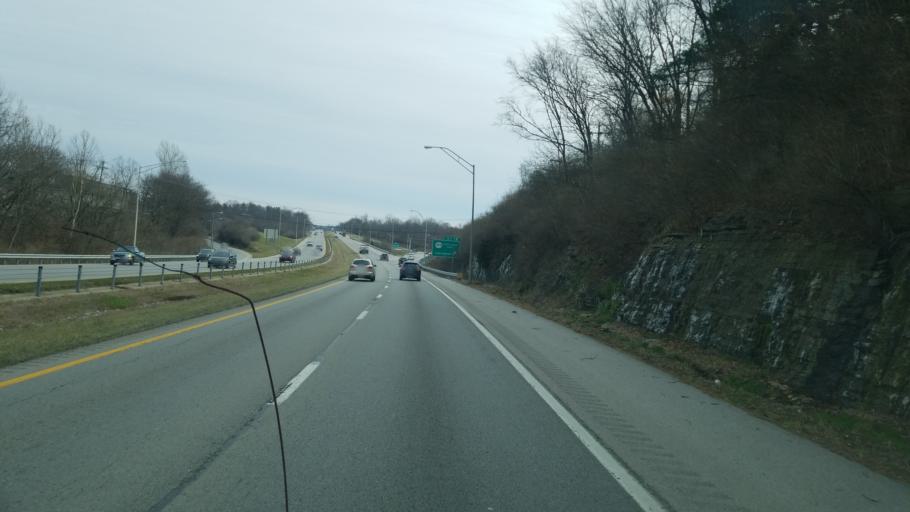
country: US
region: Kentucky
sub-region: Fayette County
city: Lexington
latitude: 37.9906
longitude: -84.5006
